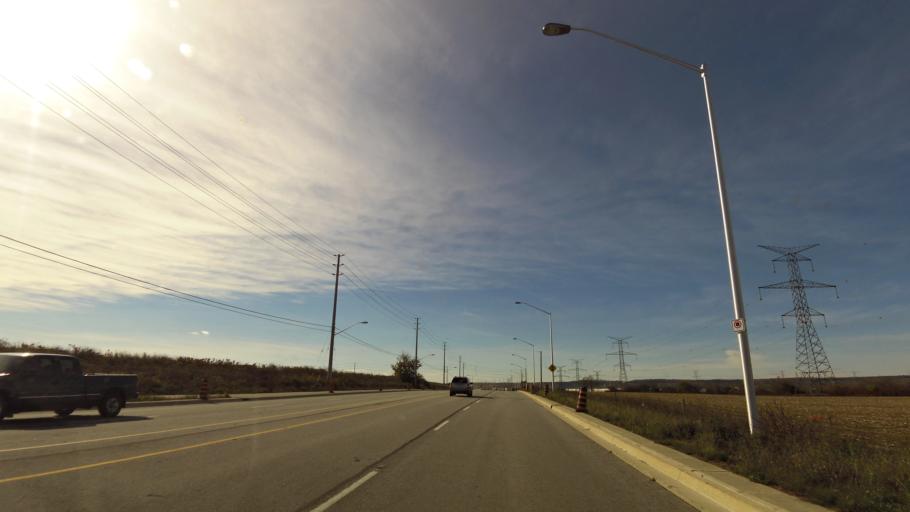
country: CA
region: Ontario
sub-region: Halton
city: Milton
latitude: 43.5429
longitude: -79.8961
